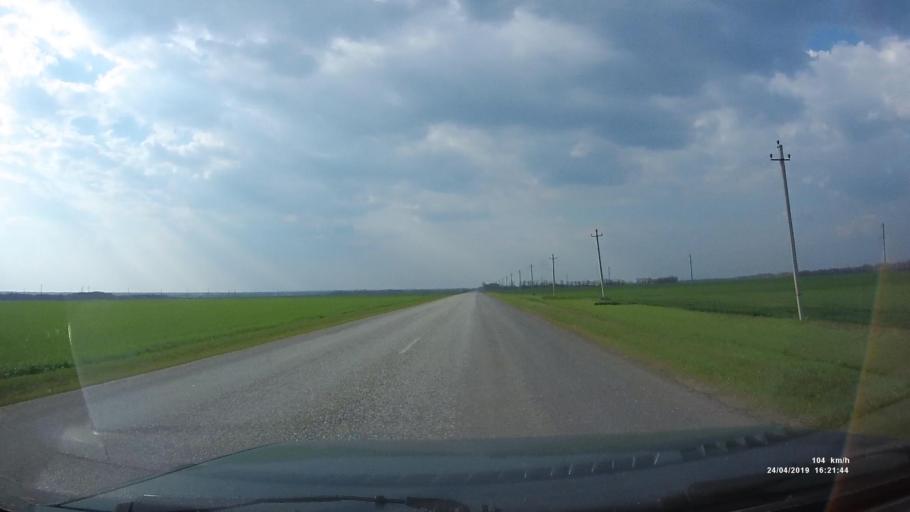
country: RU
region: Rostov
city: Orlovskiy
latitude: 46.8091
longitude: 42.0626
